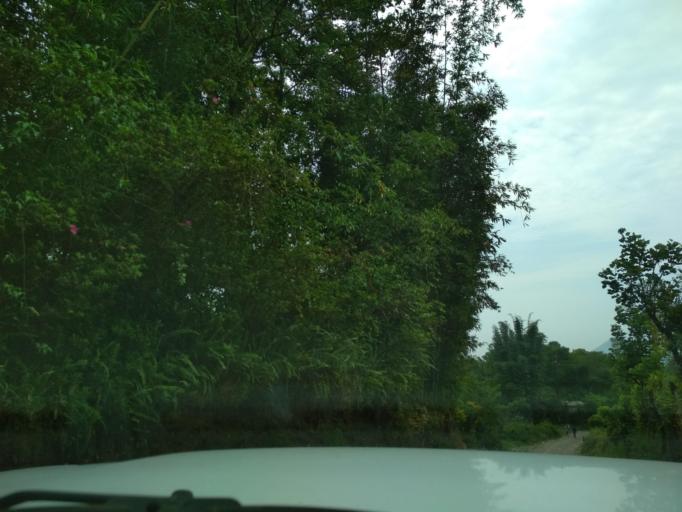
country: MX
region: Veracruz
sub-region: La Perla
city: La Perla
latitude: 18.9260
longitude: -97.1282
